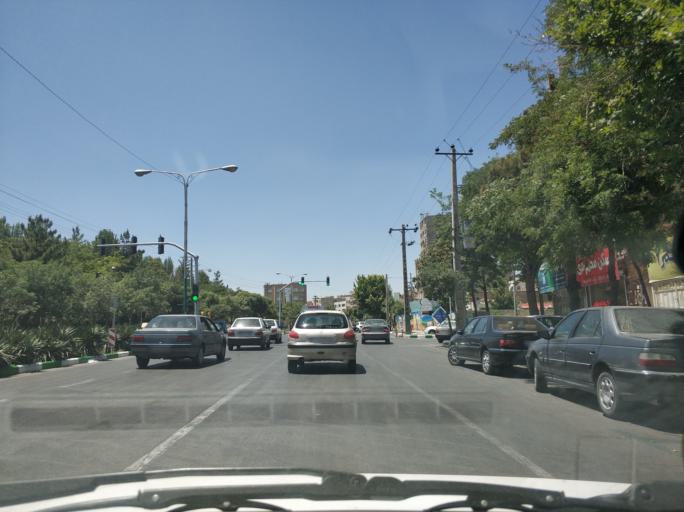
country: IR
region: Razavi Khorasan
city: Mashhad
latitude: 36.3106
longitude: 59.4977
